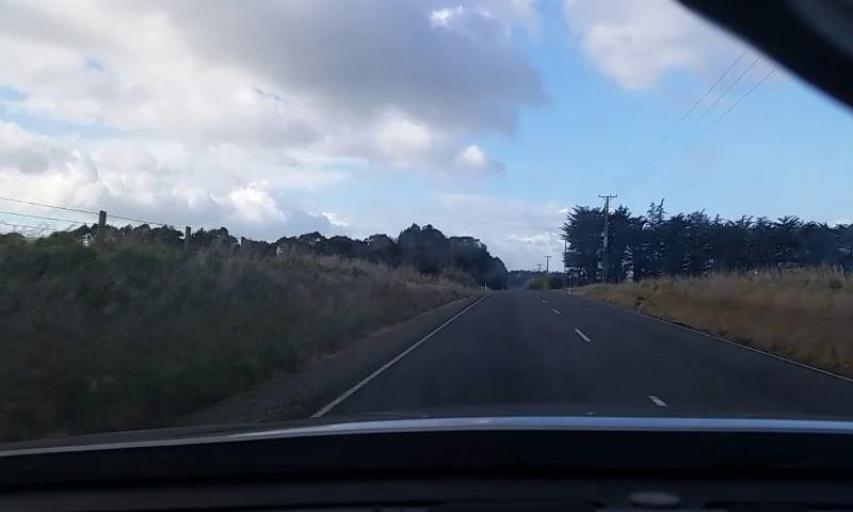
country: NZ
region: Southland
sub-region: Invercargill City
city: Invercargill
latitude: -46.3806
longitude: 168.4272
